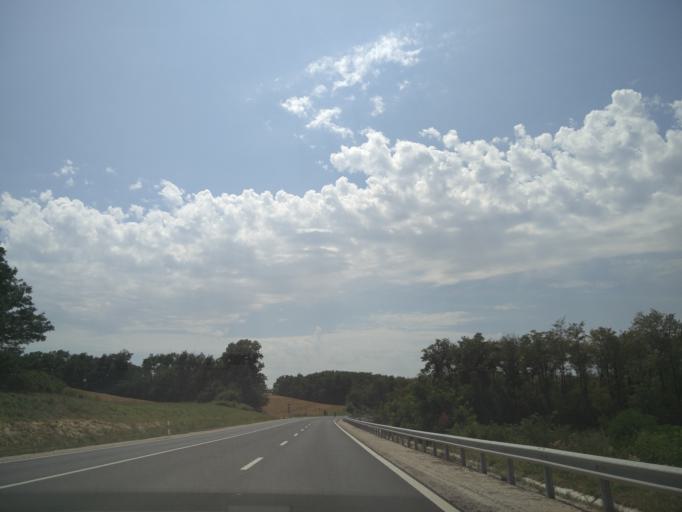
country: HU
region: Vas
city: Vasvar
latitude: 47.0690
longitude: 16.8382
